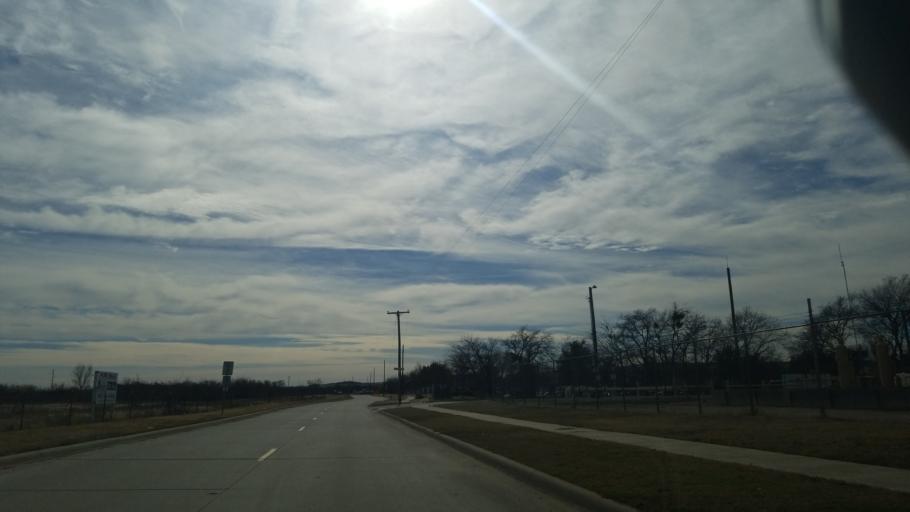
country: US
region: Texas
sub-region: Denton County
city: Denton
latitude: 33.1942
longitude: -97.1905
